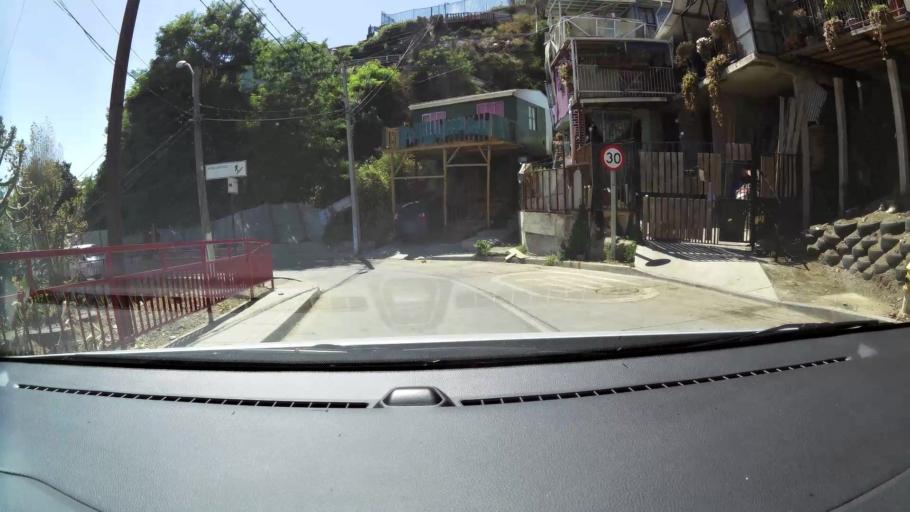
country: CL
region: Valparaiso
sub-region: Provincia de Valparaiso
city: Valparaiso
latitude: -33.0480
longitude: -71.5878
